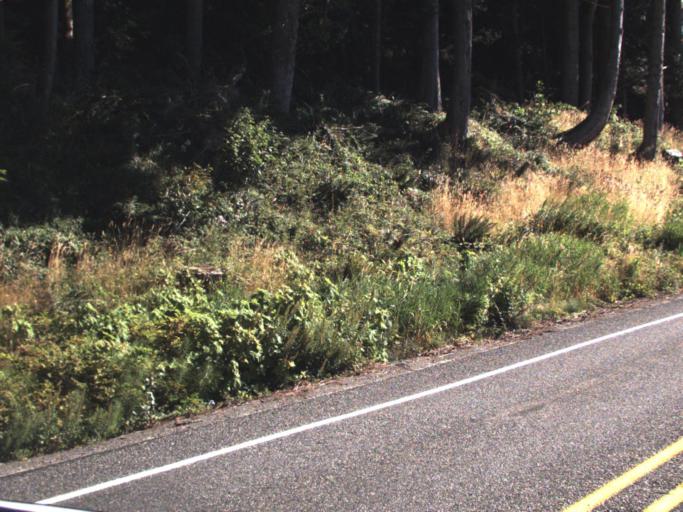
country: US
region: Washington
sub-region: King County
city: Enumclaw
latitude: 47.1539
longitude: -121.8444
